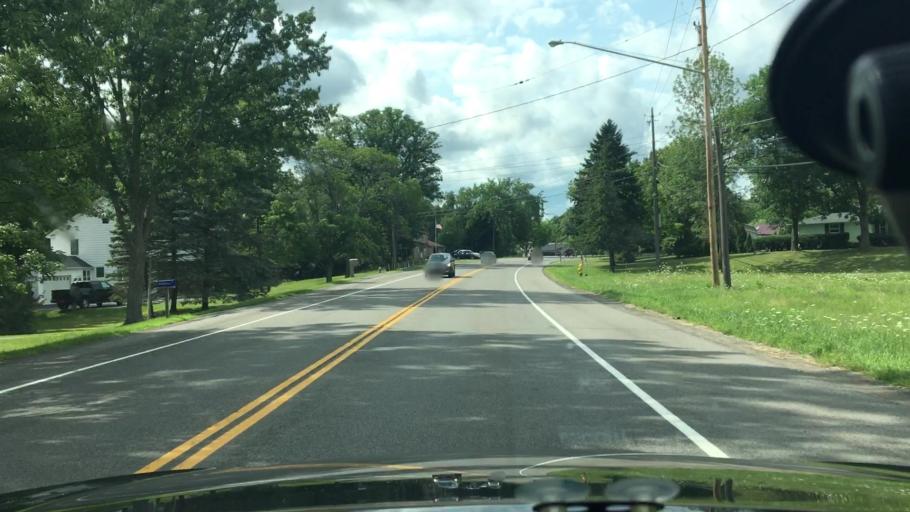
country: US
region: New York
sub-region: Erie County
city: North Boston
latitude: 42.6879
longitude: -78.7796
